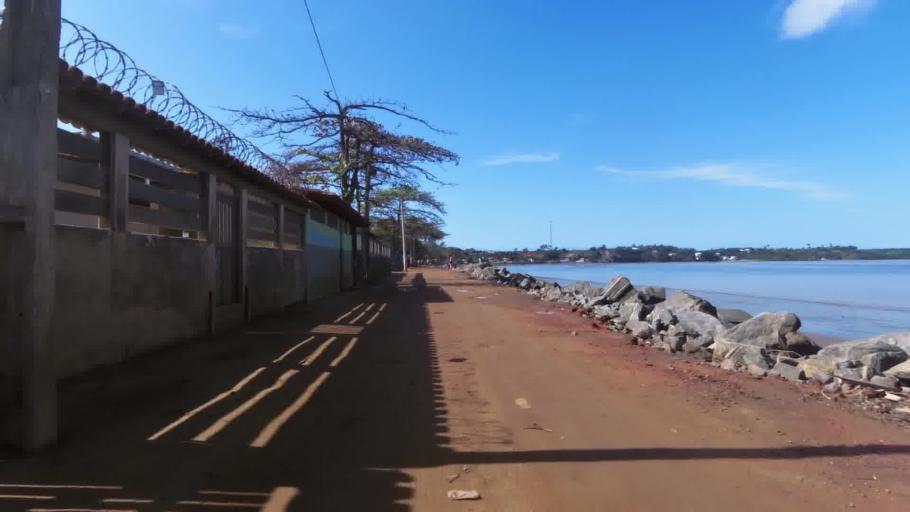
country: BR
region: Espirito Santo
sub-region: Piuma
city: Piuma
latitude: -20.8135
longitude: -40.6343
